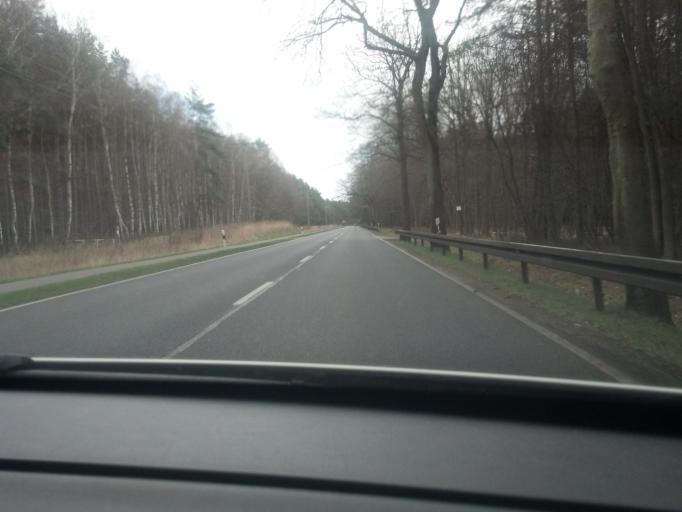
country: DE
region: Mecklenburg-Vorpommern
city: Wesenberg
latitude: 53.2710
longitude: 12.8742
